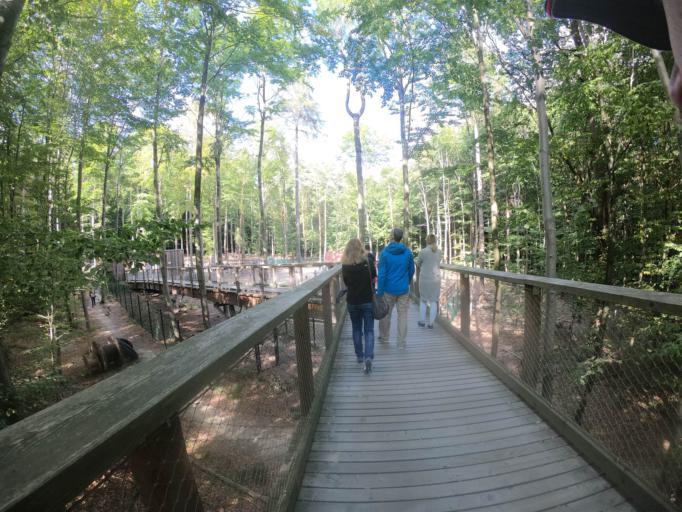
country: DE
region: Bavaria
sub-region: Regierungsbezirk Unterfranken
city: Oberschwarzach
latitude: 49.8519
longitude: 10.4601
